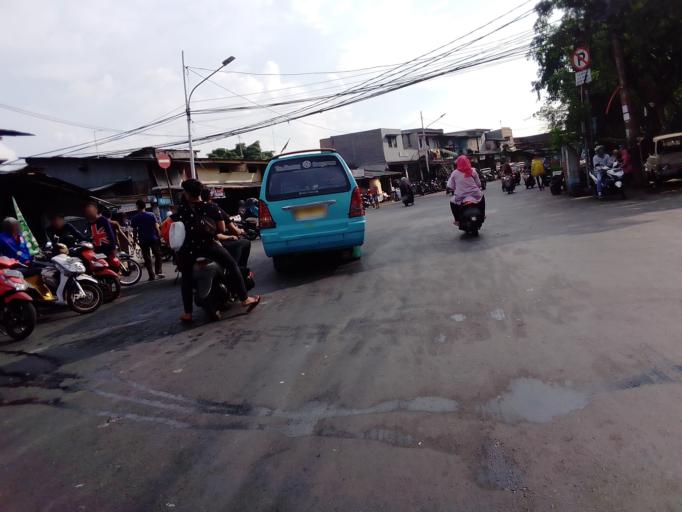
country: ID
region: Jakarta Raya
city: Jakarta
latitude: -6.1900
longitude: 106.8129
